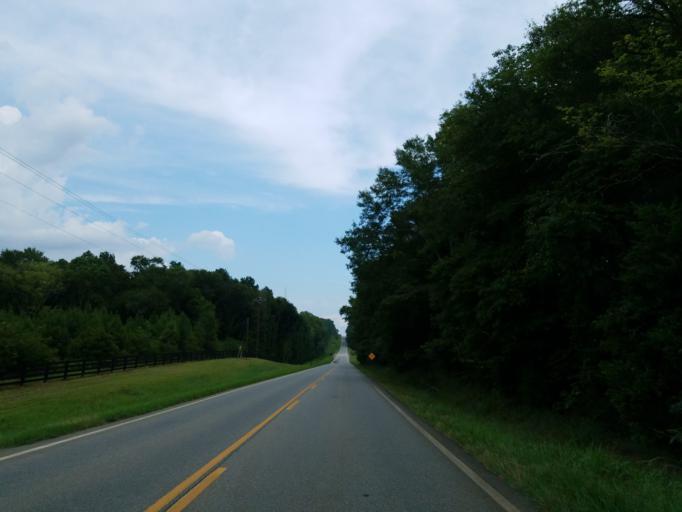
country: US
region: Georgia
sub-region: Dooly County
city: Unadilla
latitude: 32.3263
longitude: -83.7298
